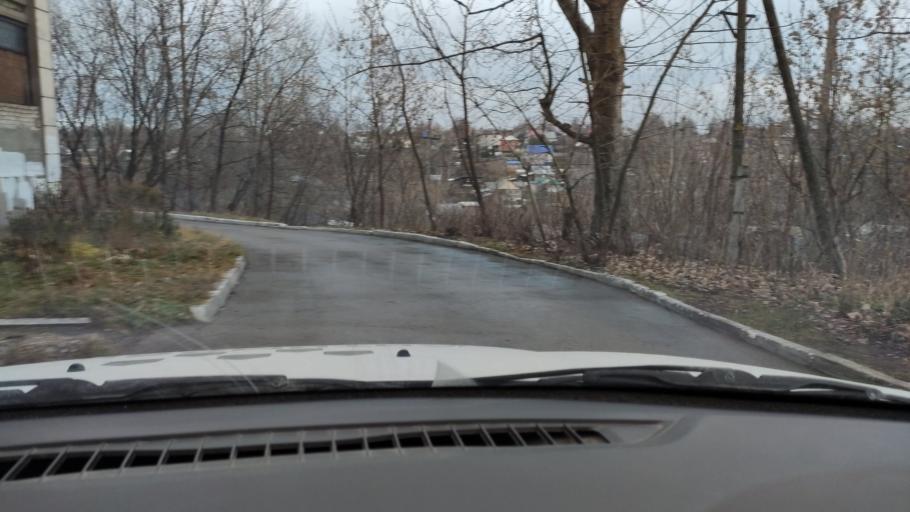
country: RU
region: Perm
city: Perm
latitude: 58.0245
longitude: 56.3064
